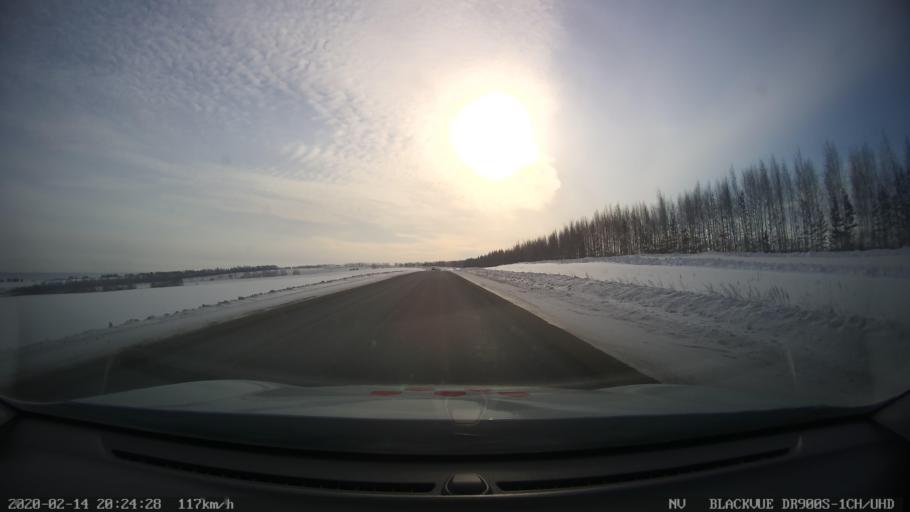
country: RU
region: Tatarstan
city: Verkhniy Uslon
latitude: 55.5119
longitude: 48.9705
